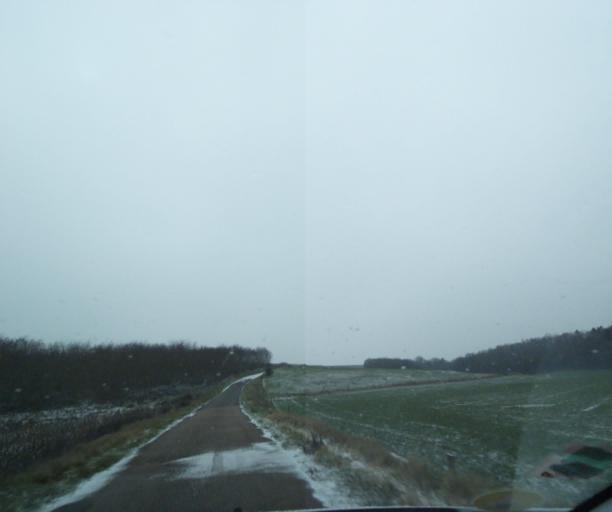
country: FR
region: Champagne-Ardenne
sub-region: Departement de la Haute-Marne
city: Wassy
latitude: 48.4653
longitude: 5.0097
